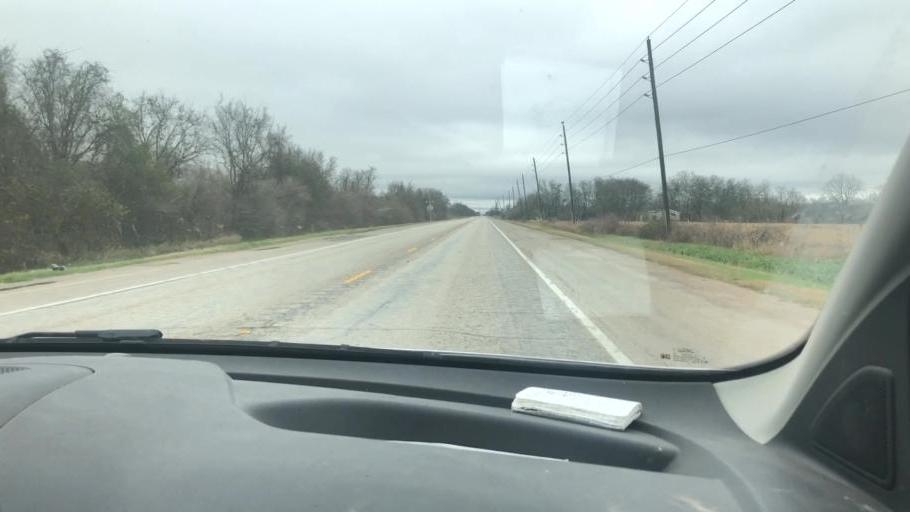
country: US
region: Texas
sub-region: Wharton County
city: Wharton
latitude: 29.2837
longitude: -96.0681
